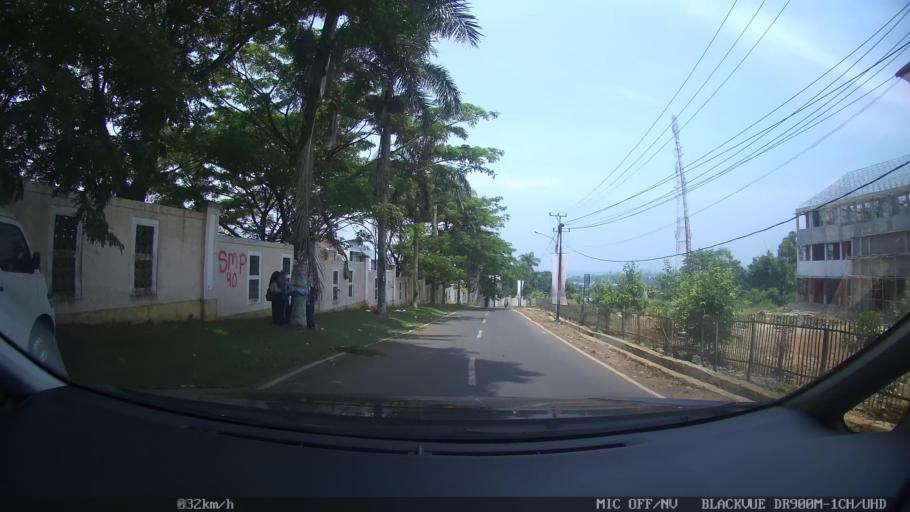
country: ID
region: Lampung
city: Bandarlampung
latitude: -5.4427
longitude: 105.2442
